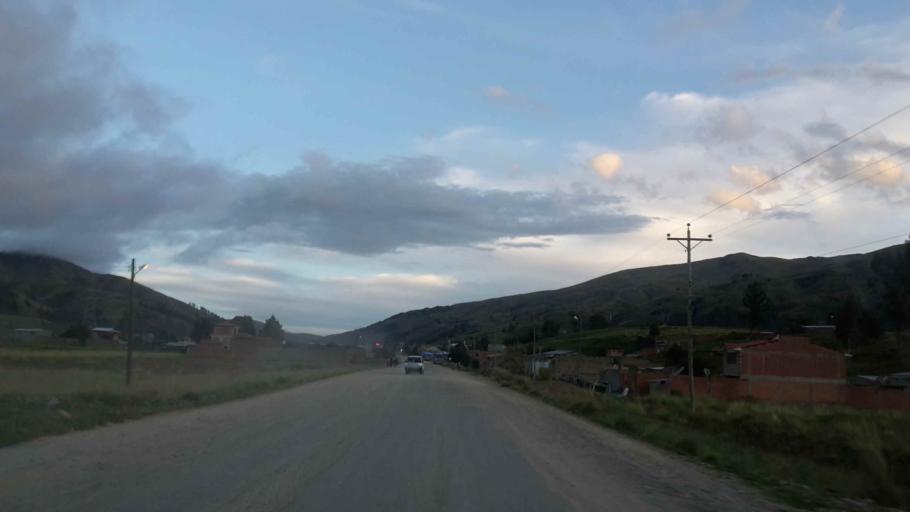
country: BO
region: Cochabamba
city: Colomi
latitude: -17.3230
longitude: -65.8775
